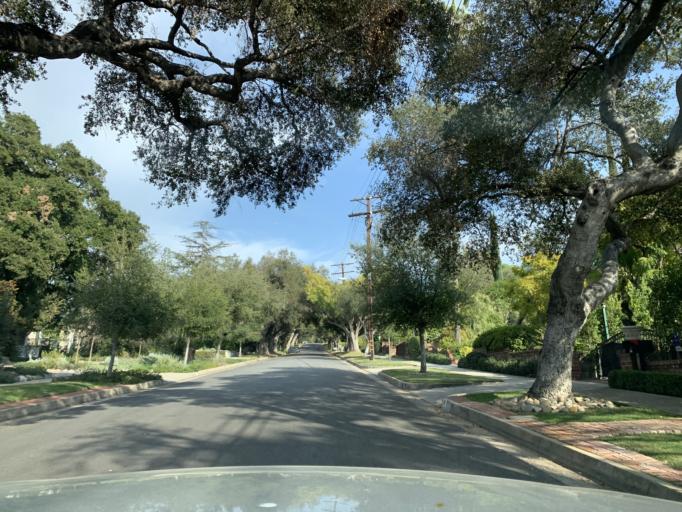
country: US
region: California
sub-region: Los Angeles County
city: South Pasadena
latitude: 34.1331
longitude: -118.1626
